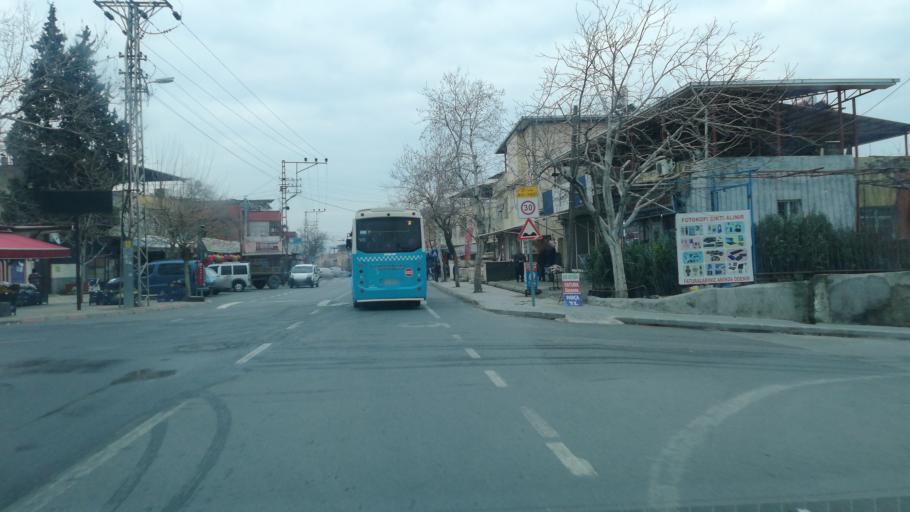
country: TR
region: Kahramanmaras
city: Kahramanmaras
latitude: 37.5713
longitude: 36.9504
